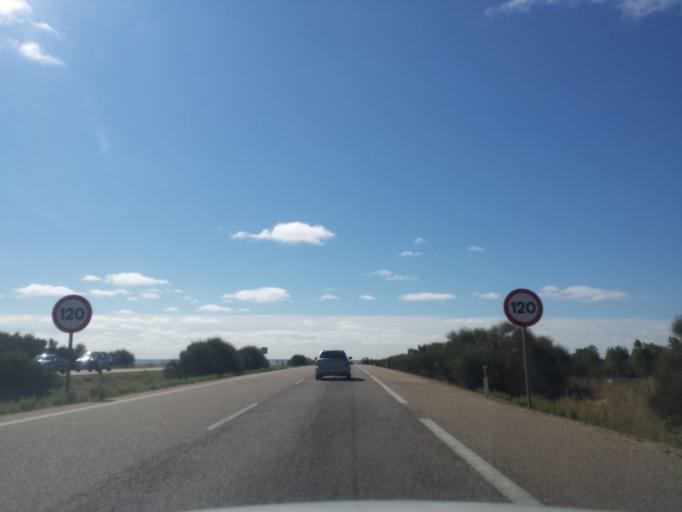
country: ES
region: Castille and Leon
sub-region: Provincia de Zamora
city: Quintanilla del Monte
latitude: 41.8226
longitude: -5.3726
